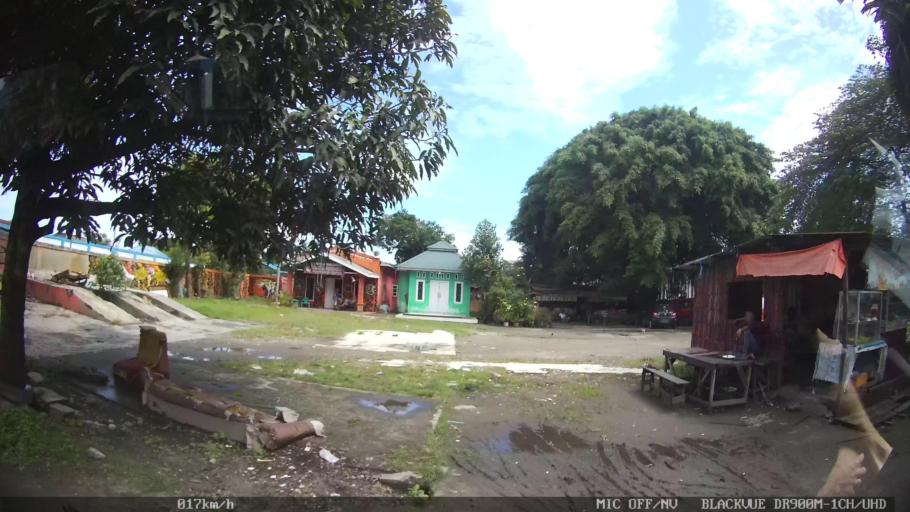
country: ID
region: North Sumatra
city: Medan
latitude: 3.5867
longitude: 98.7318
